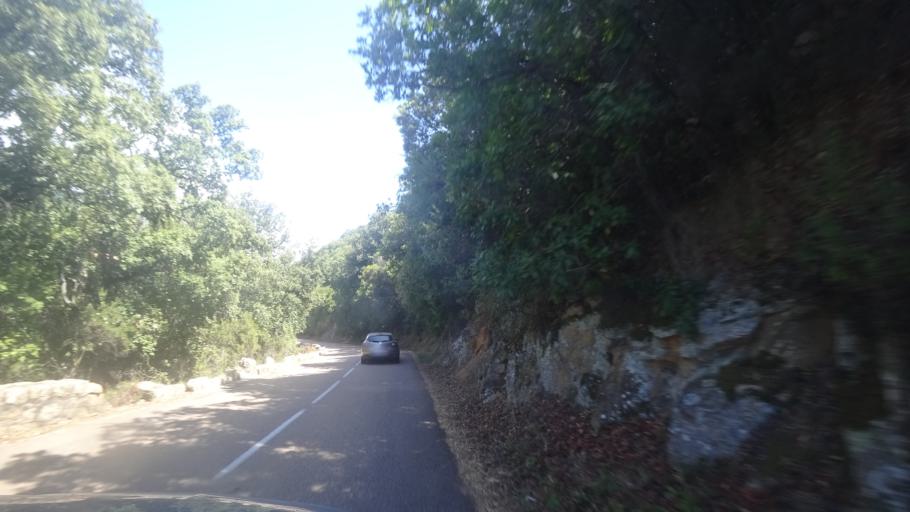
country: FR
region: Corsica
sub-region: Departement de la Corse-du-Sud
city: Cargese
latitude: 42.2627
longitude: 8.6968
